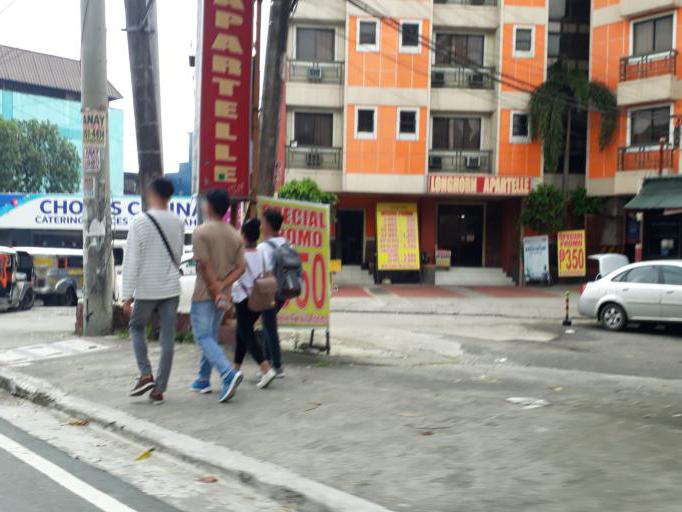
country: PH
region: Calabarzon
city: Bagong Pagasa
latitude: 14.6632
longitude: 121.0369
